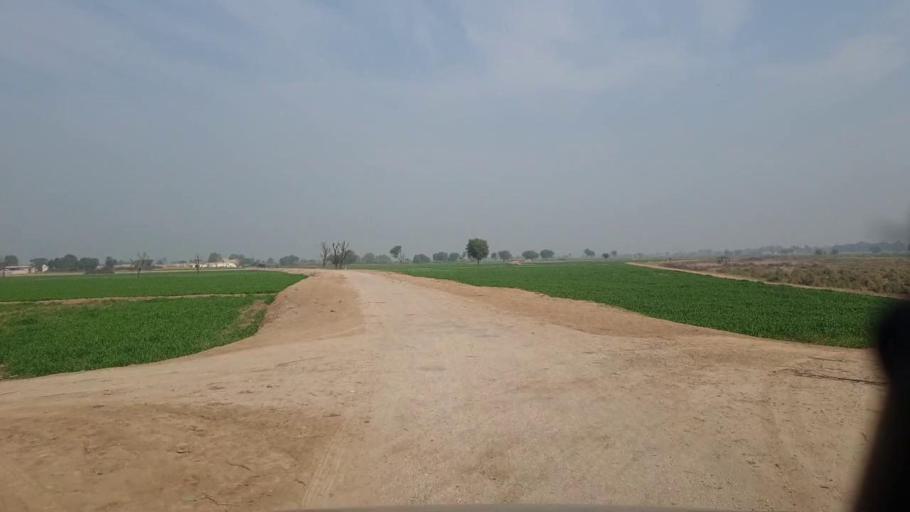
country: PK
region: Sindh
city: Shahdadpur
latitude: 26.0091
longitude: 68.5099
